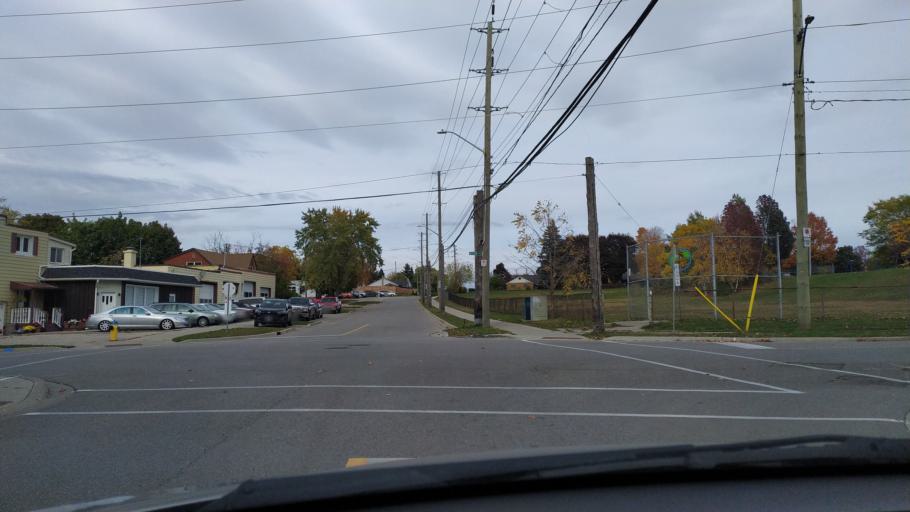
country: CA
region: Ontario
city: Waterloo
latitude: 43.4653
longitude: -80.5136
